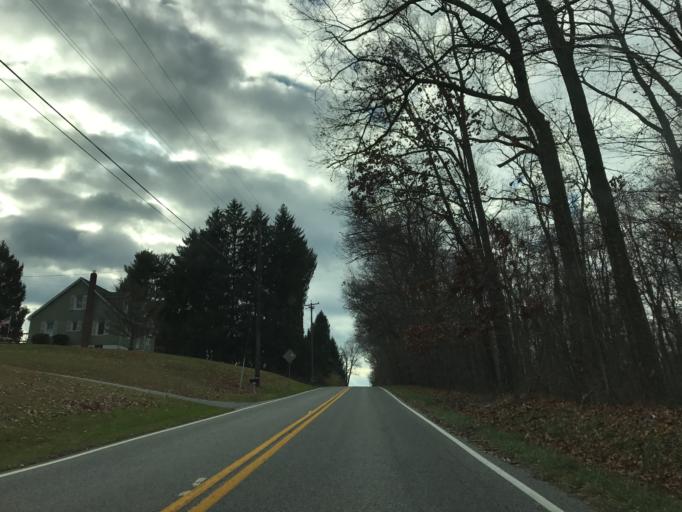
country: US
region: Pennsylvania
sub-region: York County
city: Stewartstown
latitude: 39.6579
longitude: -76.6059
